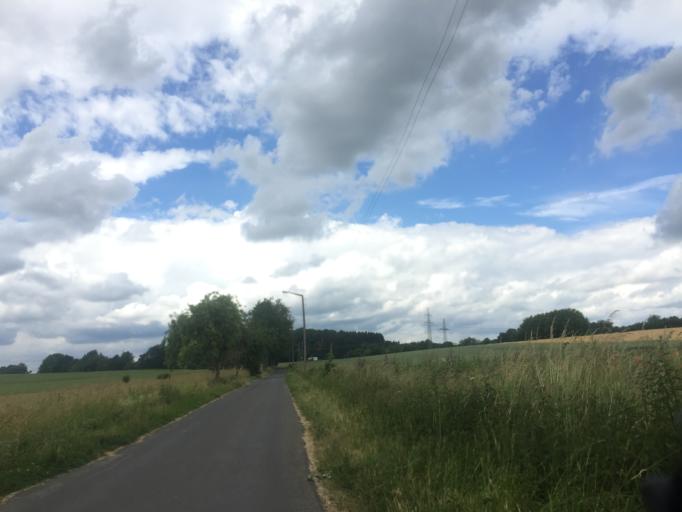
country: DE
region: Rheinland-Pfalz
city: Girod
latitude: 50.4526
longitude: 7.9048
